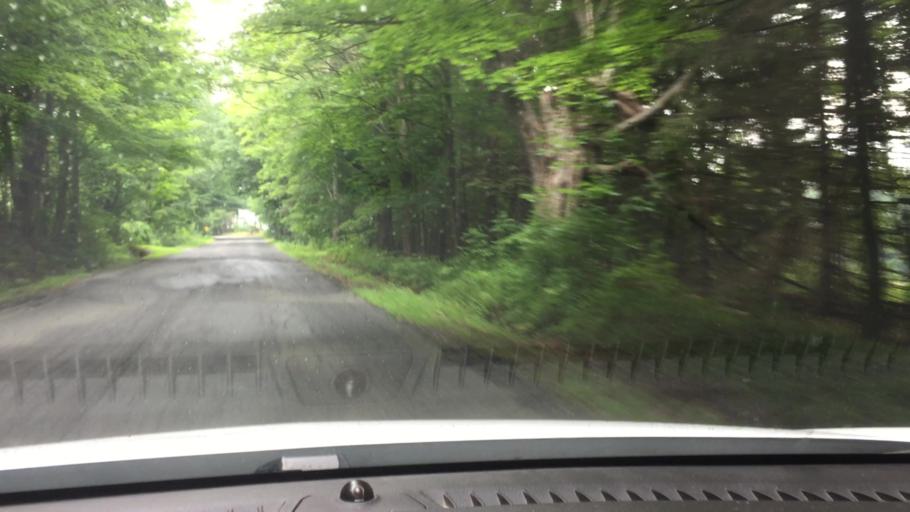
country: US
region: Massachusetts
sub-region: Berkshire County
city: Lee
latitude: 42.3007
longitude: -73.2801
